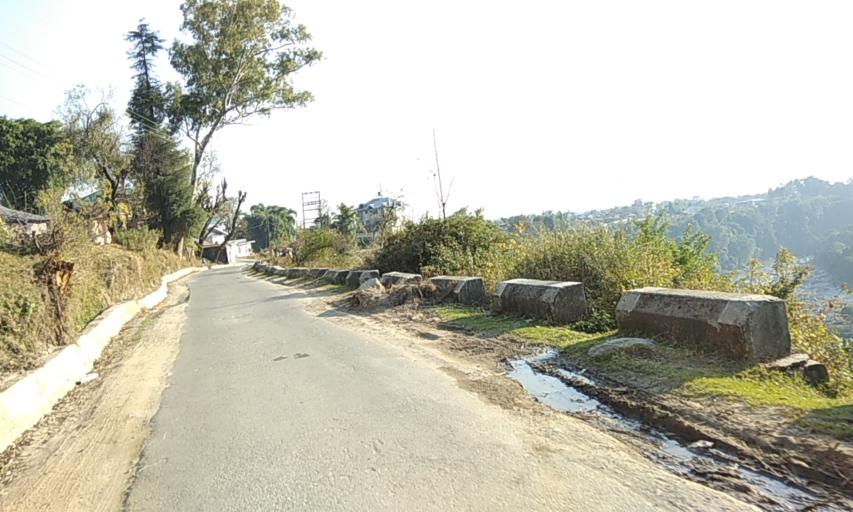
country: IN
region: Himachal Pradesh
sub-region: Kangra
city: Palampur
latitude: 32.1335
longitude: 76.5355
